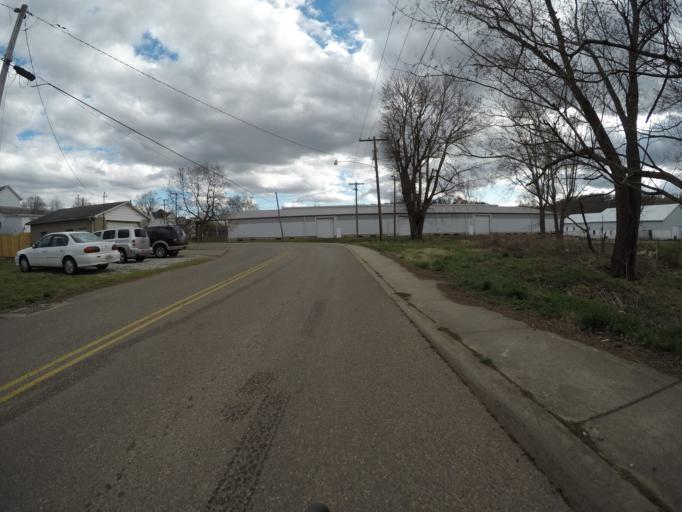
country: US
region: Ohio
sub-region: Washington County
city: Marietta
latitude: 39.4289
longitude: -81.4672
